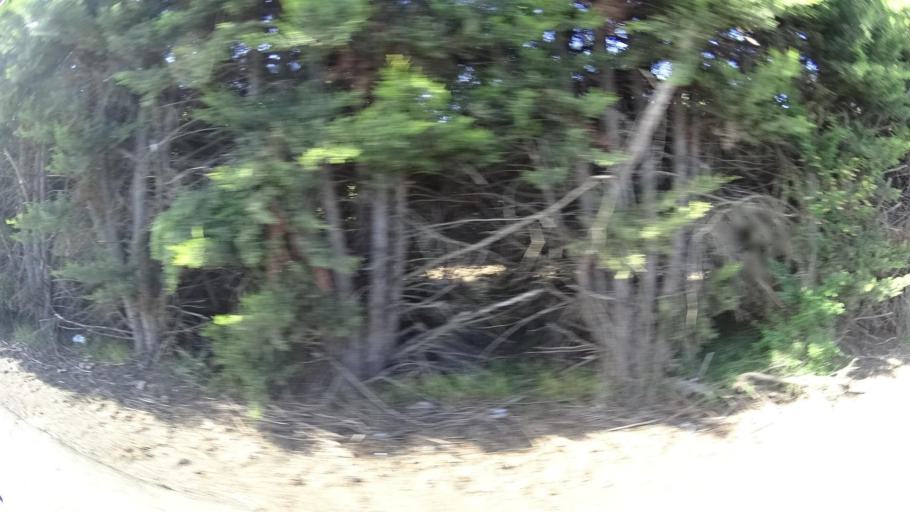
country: US
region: California
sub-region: Lake County
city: Lakeport
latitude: 39.0623
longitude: -122.9409
